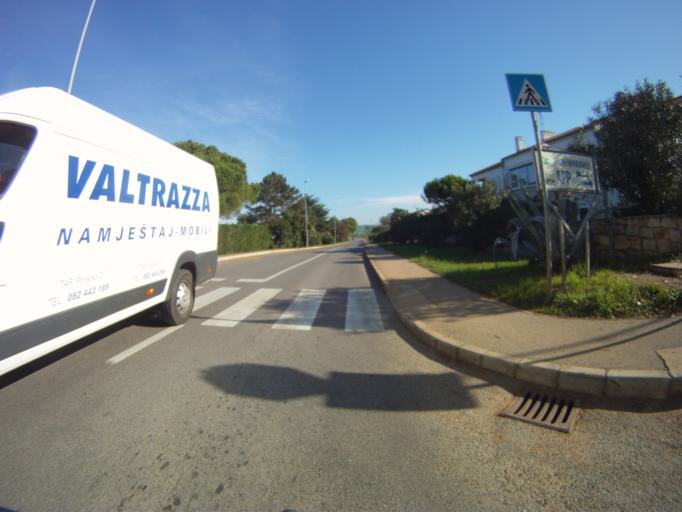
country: HR
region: Istarska
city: Novigrad
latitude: 45.3525
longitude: 13.5497
